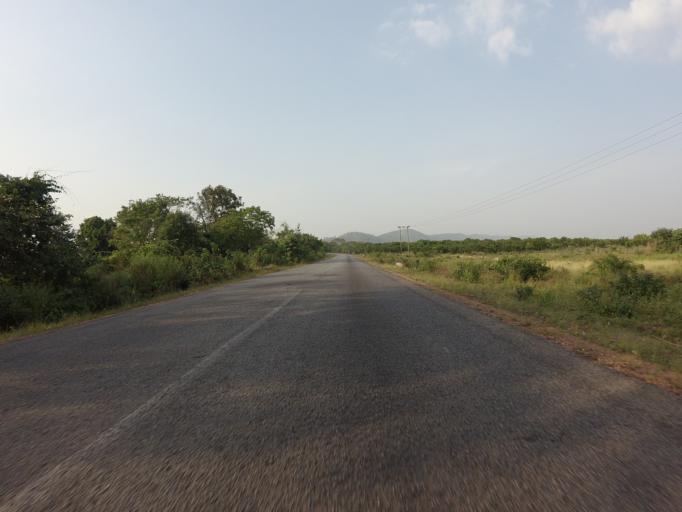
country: GH
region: Volta
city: Ho
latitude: 6.3996
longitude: 0.1783
